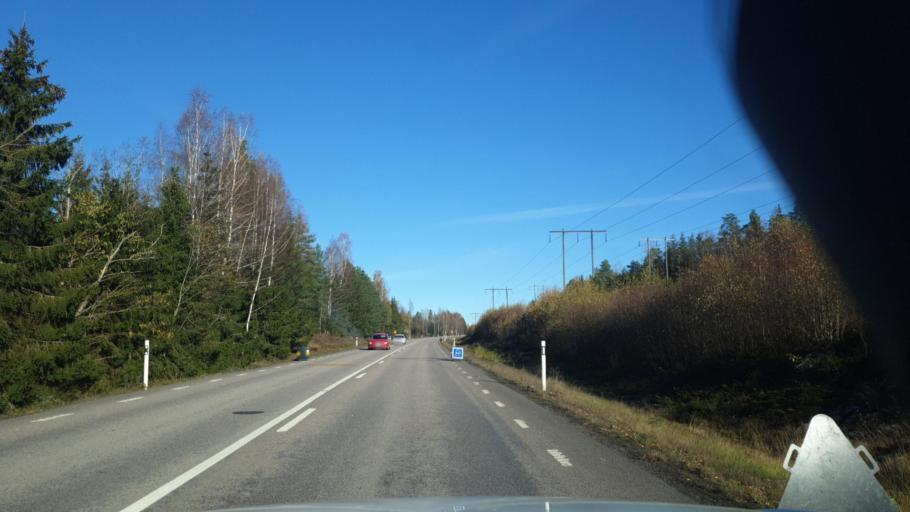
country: SE
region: Vaermland
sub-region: Karlstads Kommun
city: Valberg
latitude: 59.4083
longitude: 13.1836
